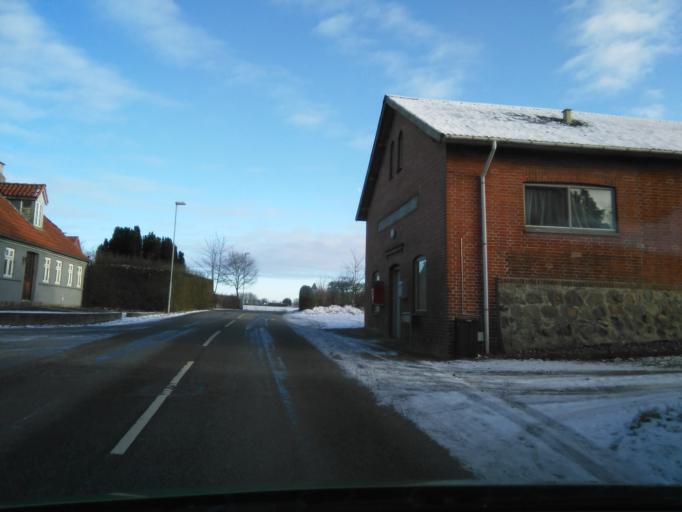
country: DK
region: Central Jutland
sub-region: Skanderborg Kommune
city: Skovby
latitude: 56.1479
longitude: 9.9799
